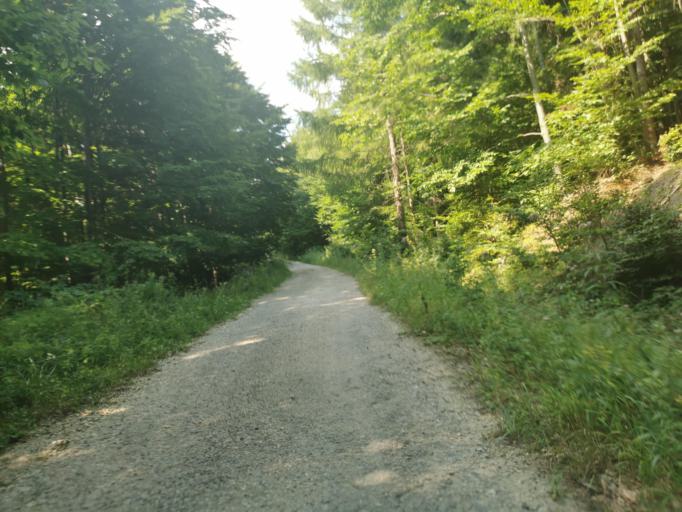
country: SK
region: Trenciansky
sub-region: Okres Myjava
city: Myjava
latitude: 48.8170
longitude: 17.5642
